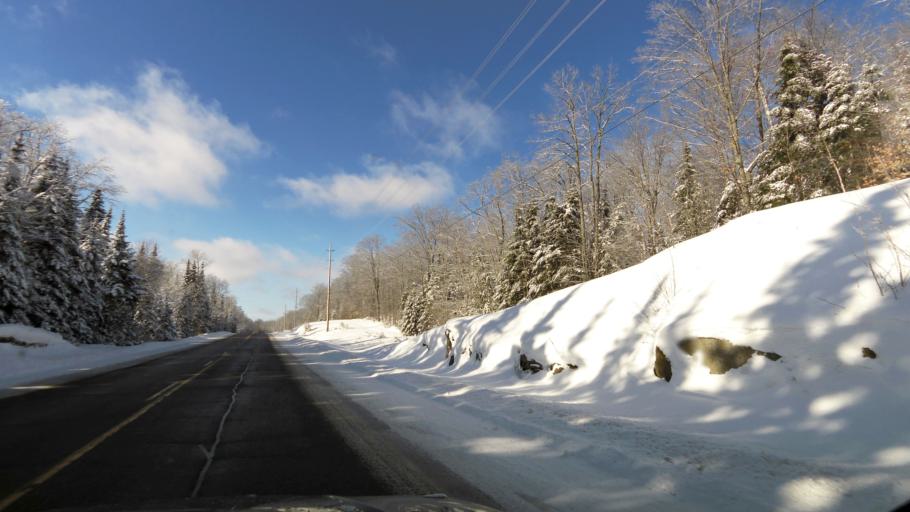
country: CA
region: Ontario
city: Bancroft
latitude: 45.0118
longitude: -78.3260
